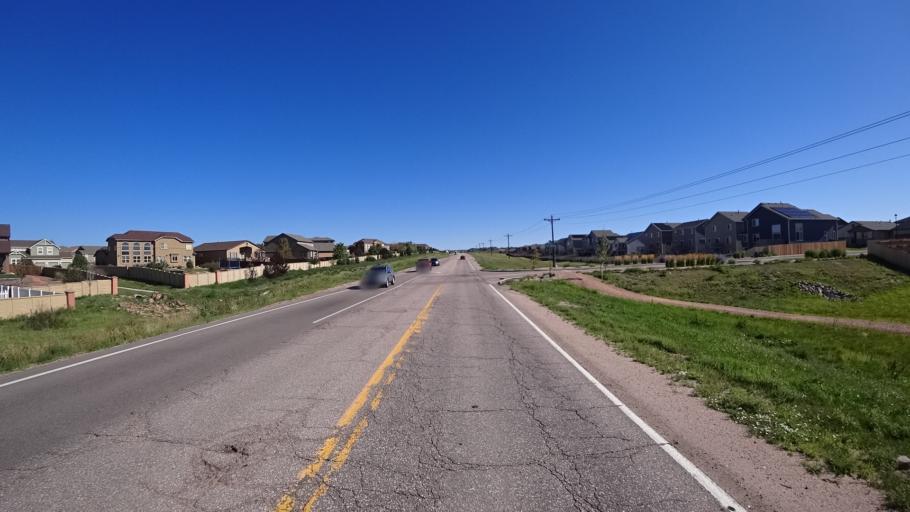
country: US
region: Colorado
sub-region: El Paso County
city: Cimarron Hills
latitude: 38.9186
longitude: -104.6828
